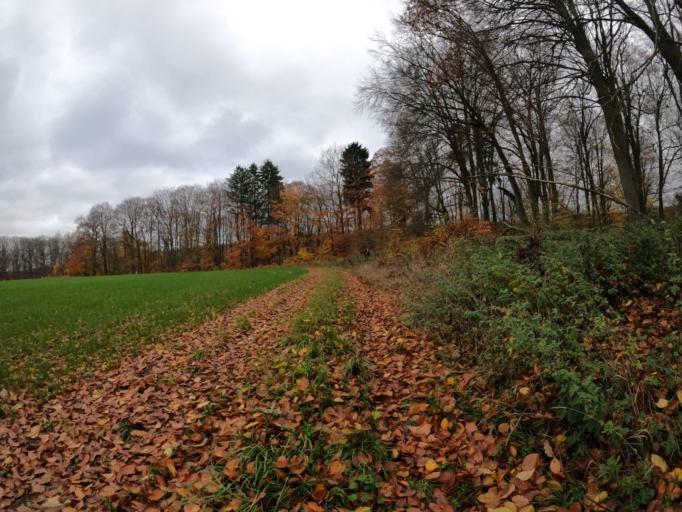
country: PL
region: West Pomeranian Voivodeship
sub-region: Powiat walecki
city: Tuczno
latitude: 53.2530
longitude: 16.2394
